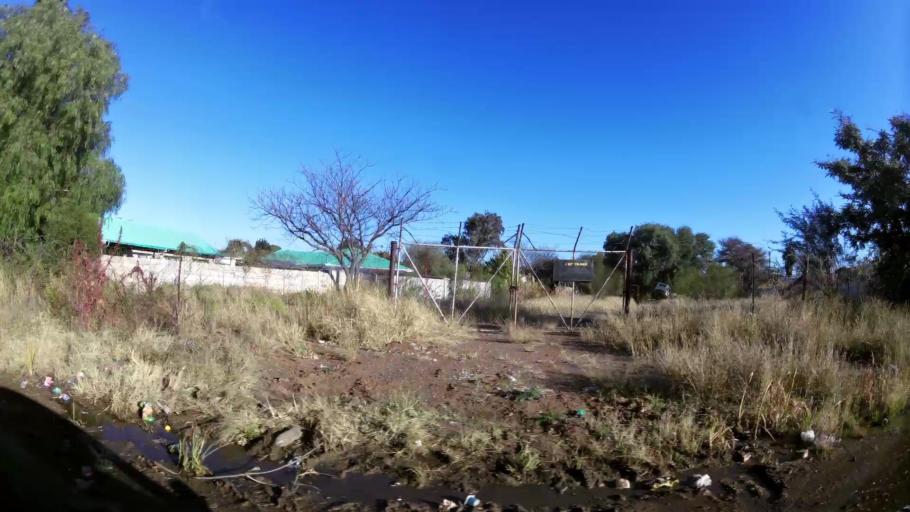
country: ZA
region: Northern Cape
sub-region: Frances Baard District Municipality
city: Kimberley
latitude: -28.7408
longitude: 24.7387
